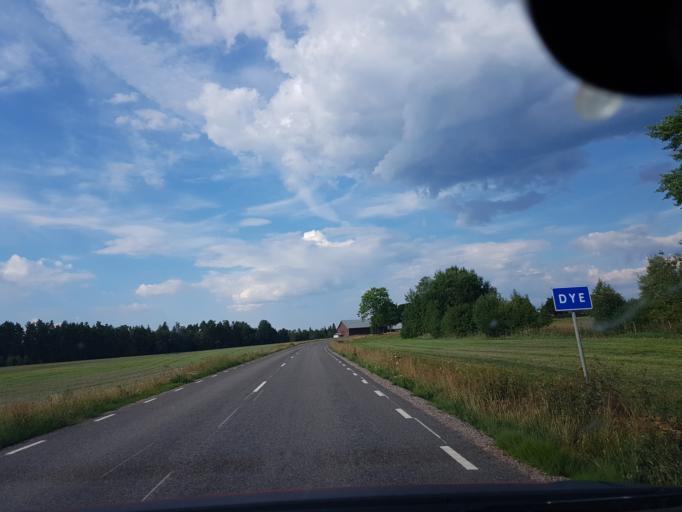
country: SE
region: Joenkoeping
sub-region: Gislaveds Kommun
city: Reftele
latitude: 57.2047
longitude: 13.5995
